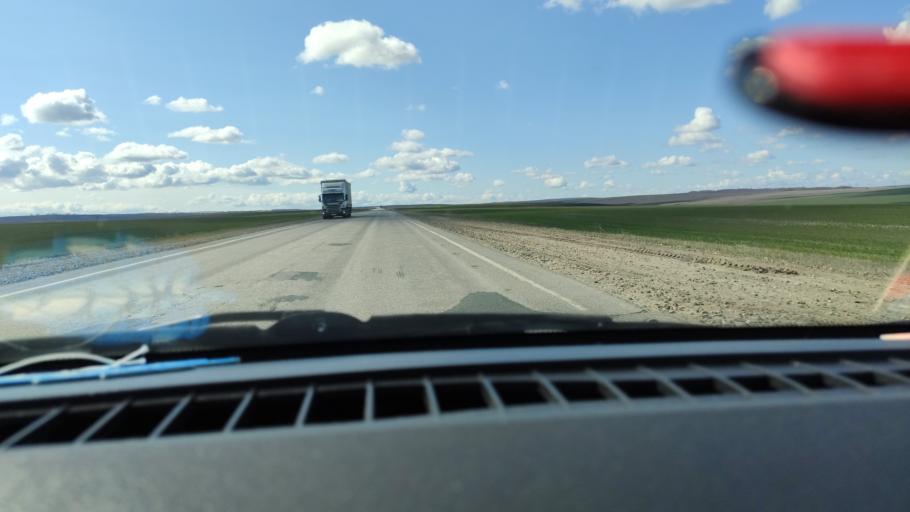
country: RU
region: Samara
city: Varlamovo
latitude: 53.0473
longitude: 48.3430
